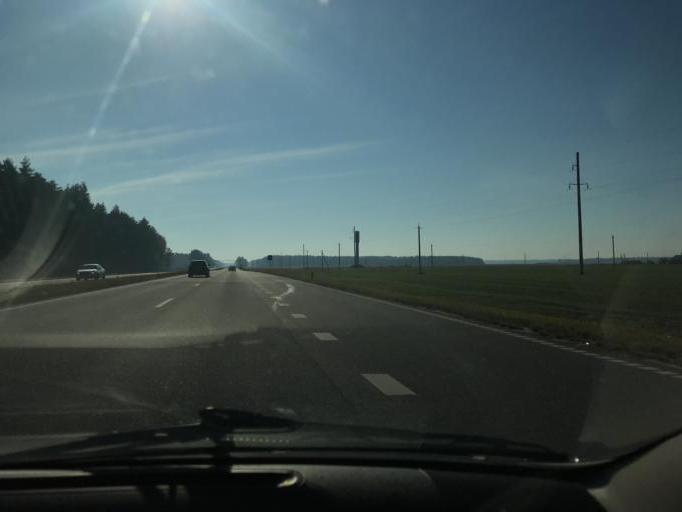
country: BY
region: Minsk
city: Slutsk
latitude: 53.3236
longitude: 27.5332
